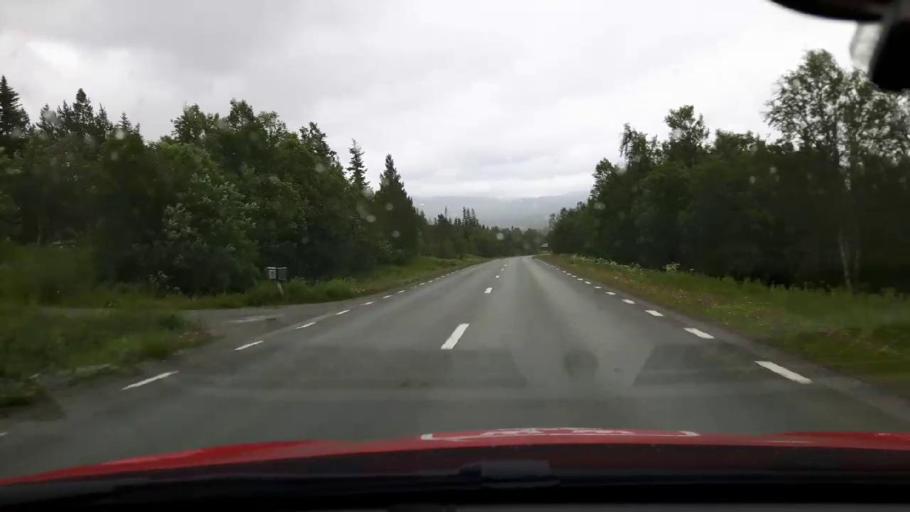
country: NO
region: Nord-Trondelag
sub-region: Meraker
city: Meraker
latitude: 63.2961
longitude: 12.1151
